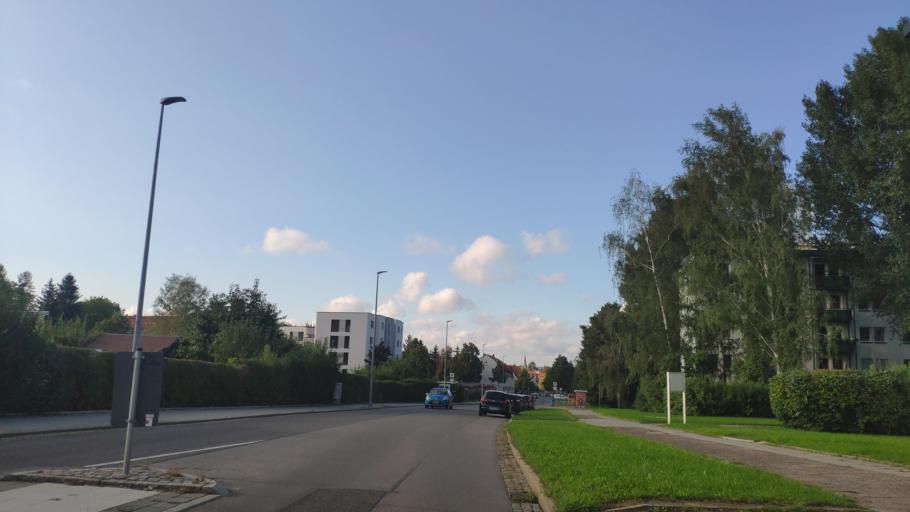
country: DE
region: Saxony
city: Chemnitz
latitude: 50.8202
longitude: 12.9575
